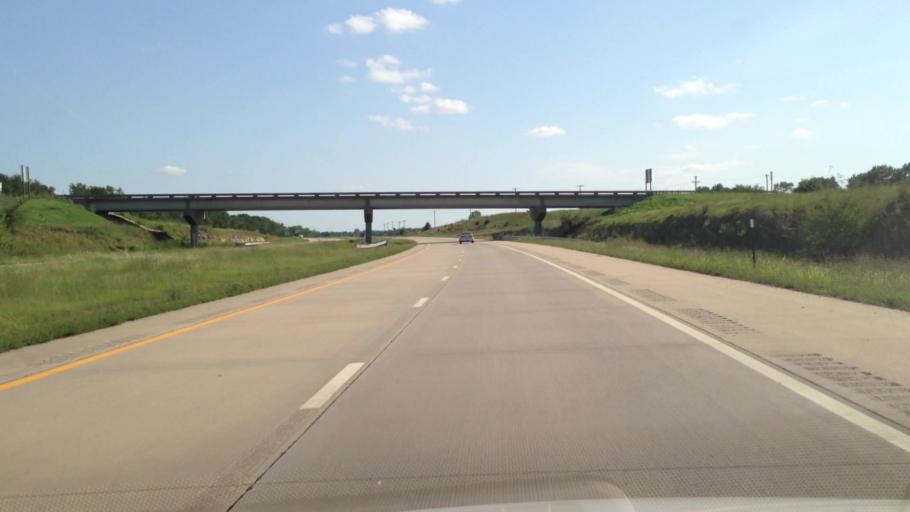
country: US
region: Kansas
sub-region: Bourbon County
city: Fort Scott
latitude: 37.8936
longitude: -94.7055
